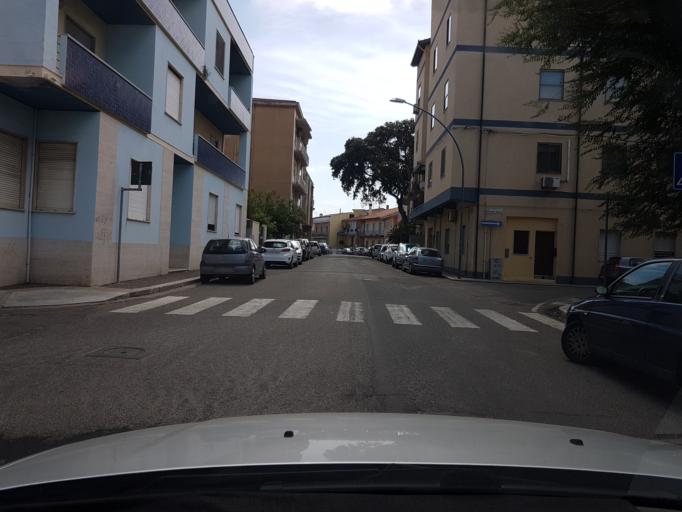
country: IT
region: Sardinia
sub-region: Provincia di Oristano
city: Oristano
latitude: 39.9082
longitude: 8.5955
